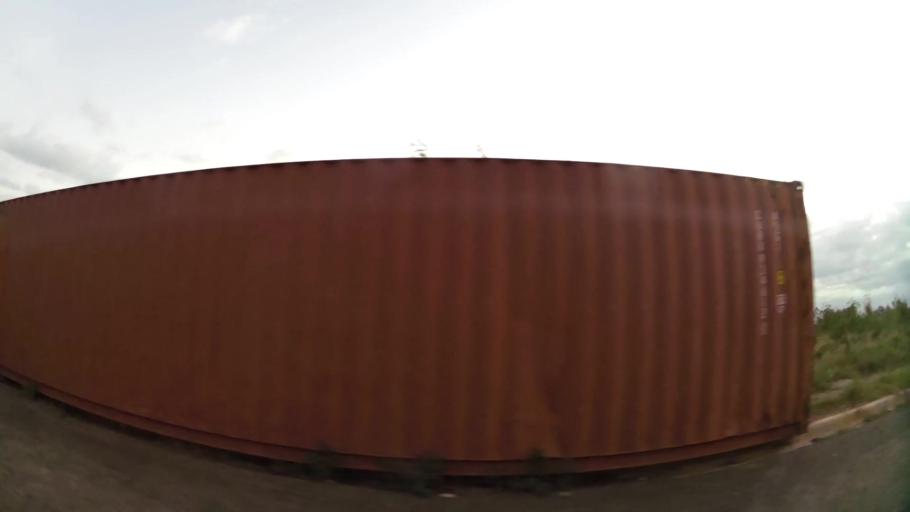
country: DO
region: Nacional
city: La Agustina
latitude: 18.5422
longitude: -69.9429
